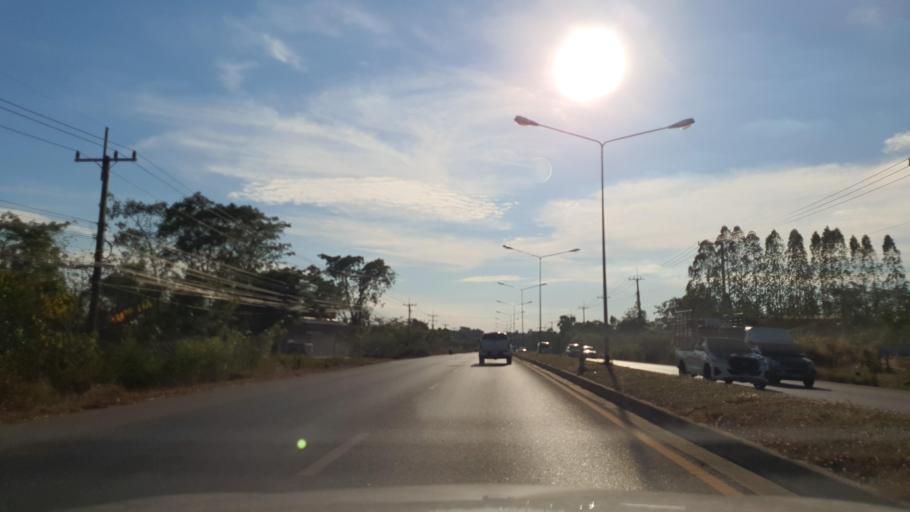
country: TH
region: Maha Sarakham
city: Kantharawichai
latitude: 16.3404
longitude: 103.3143
